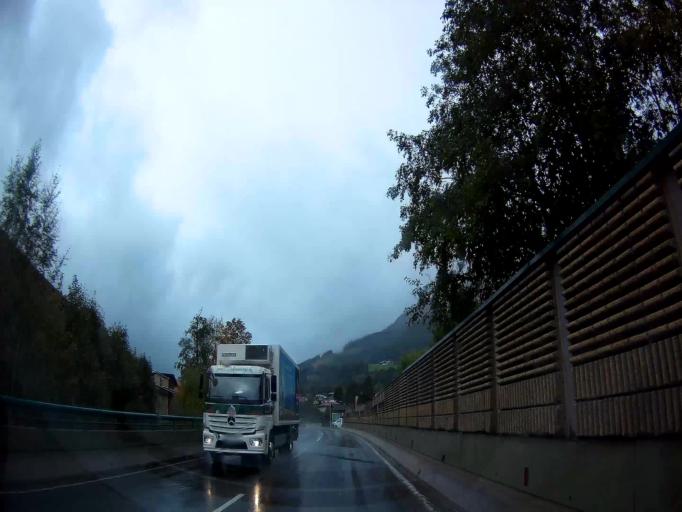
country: AT
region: Salzburg
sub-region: Politischer Bezirk Zell am See
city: Leogang
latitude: 47.4401
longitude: 12.7438
